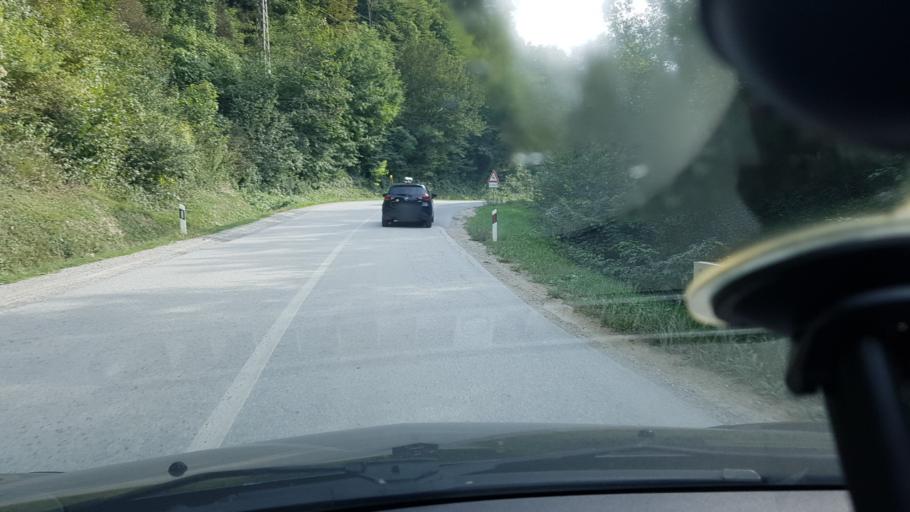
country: HR
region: Varazdinska
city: Lepoglava
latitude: 46.1887
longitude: 15.9854
